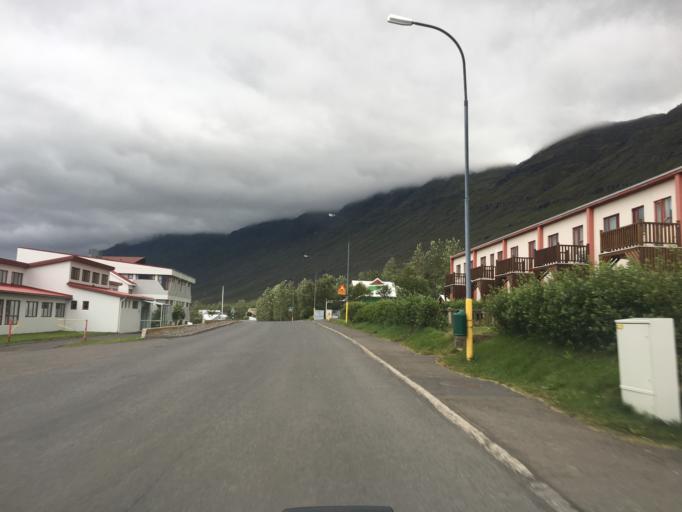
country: IS
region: East
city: Neskaupstadur
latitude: 65.1490
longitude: -13.6781
